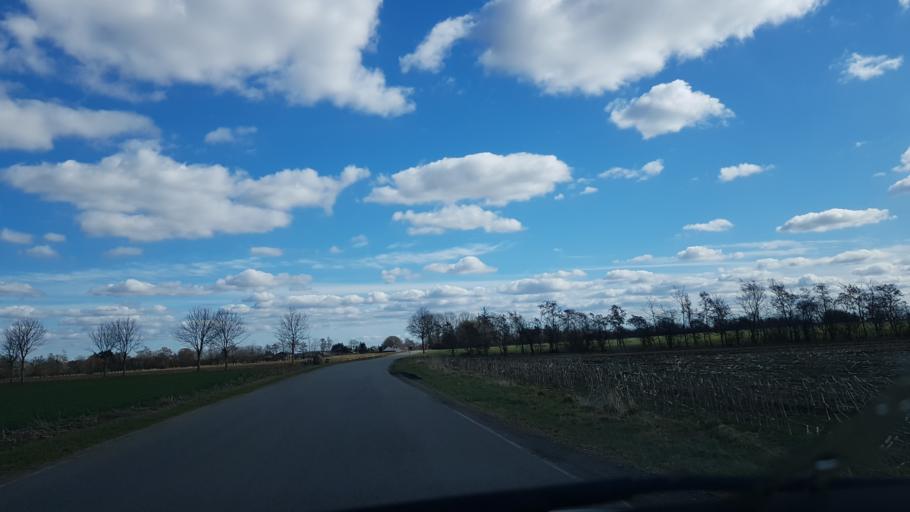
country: DK
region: South Denmark
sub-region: Vejen Kommune
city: Rodding
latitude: 55.3941
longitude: 9.0282
